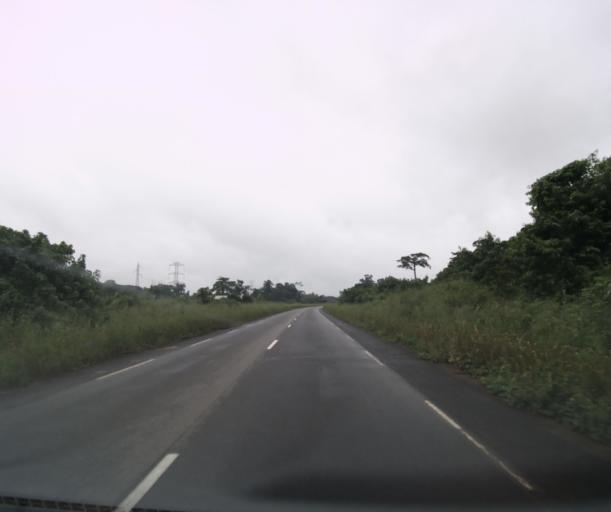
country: CM
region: Littoral
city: Edea
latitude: 3.4810
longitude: 10.1303
